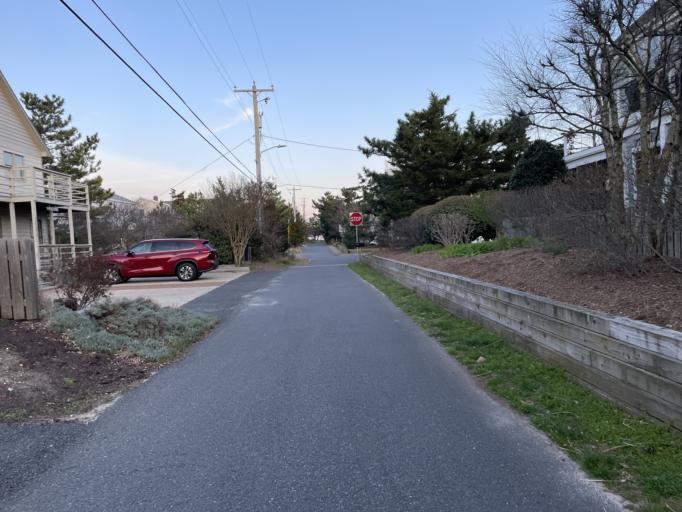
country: US
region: Delaware
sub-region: Sussex County
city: Lewes
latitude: 38.7872
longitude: -75.1538
